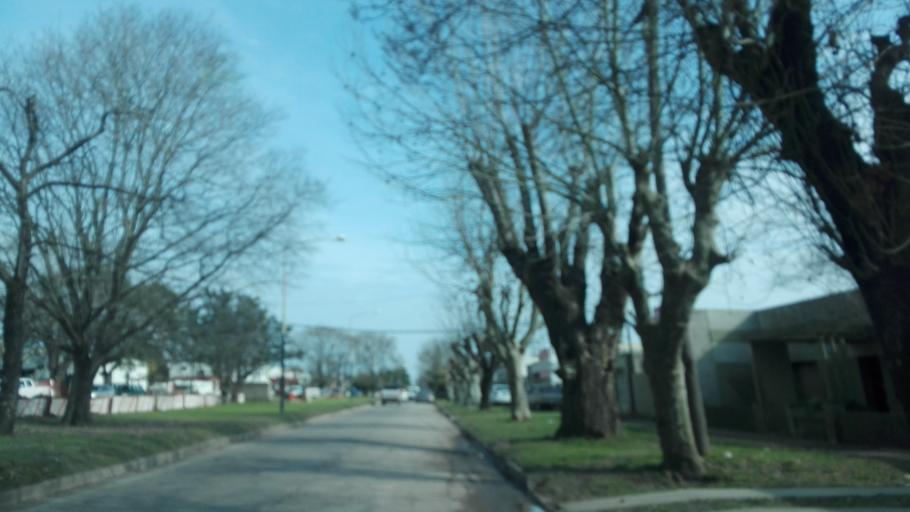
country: AR
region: Buenos Aires
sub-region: Partido de Chascomus
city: Chascomus
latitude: -35.5678
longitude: -58.0130
